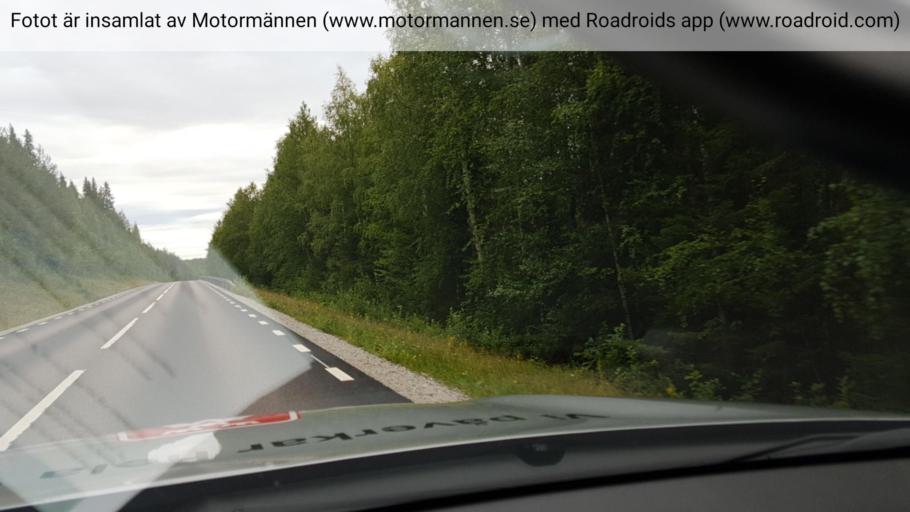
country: SE
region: Norrbotten
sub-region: Overkalix Kommun
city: OEverkalix
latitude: 66.4672
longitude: 22.7927
